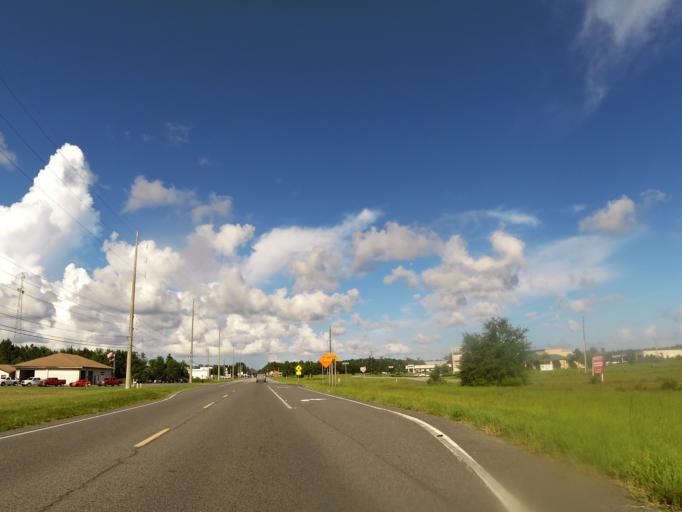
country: US
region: Georgia
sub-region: Glynn County
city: Dock Junction
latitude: 31.1392
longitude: -81.5899
